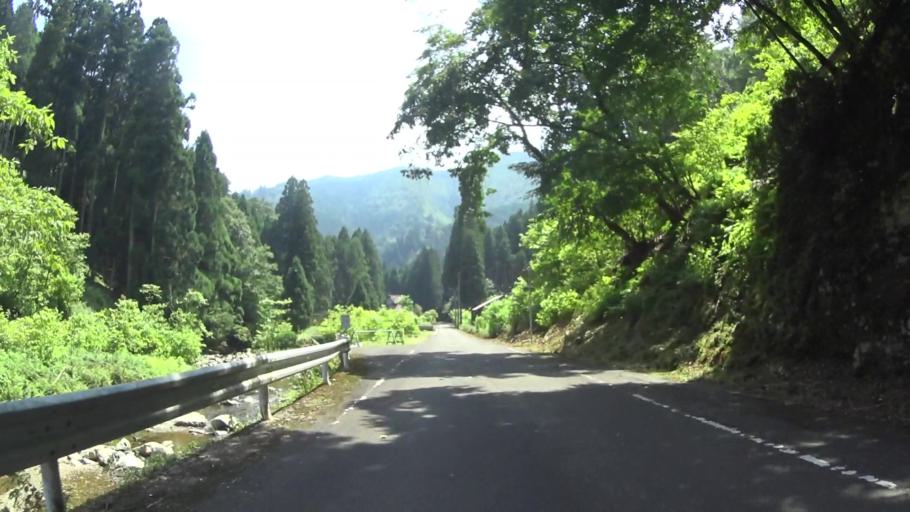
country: JP
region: Kyoto
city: Maizuru
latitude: 35.3464
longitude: 135.5243
